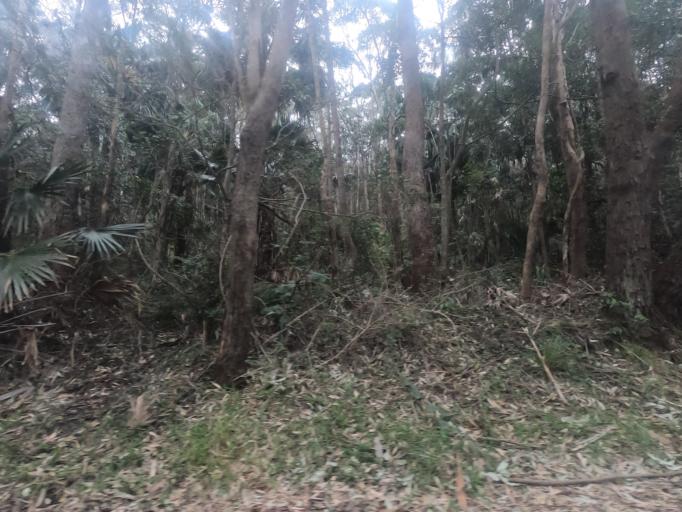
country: AU
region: New South Wales
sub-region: Wollongong
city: Bulli
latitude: -34.2980
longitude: 150.9317
